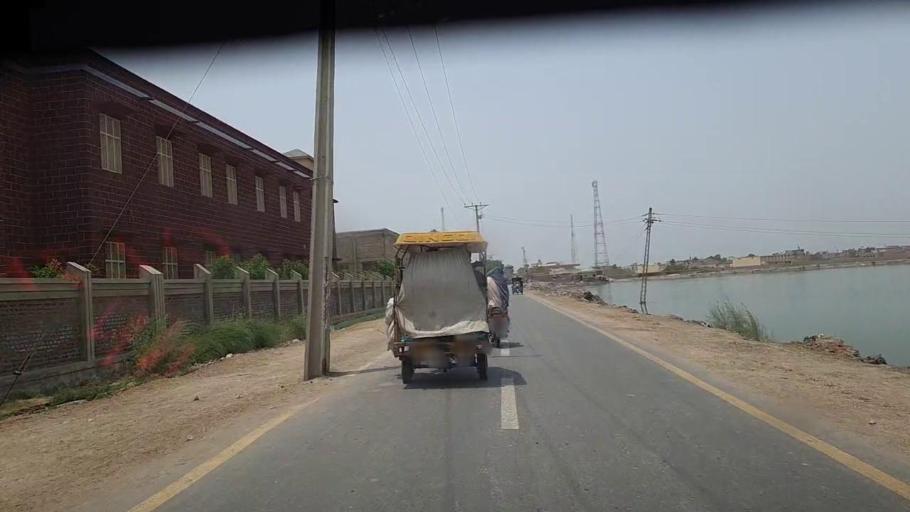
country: PK
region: Sindh
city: Sita Road
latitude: 27.0413
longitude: 67.8549
